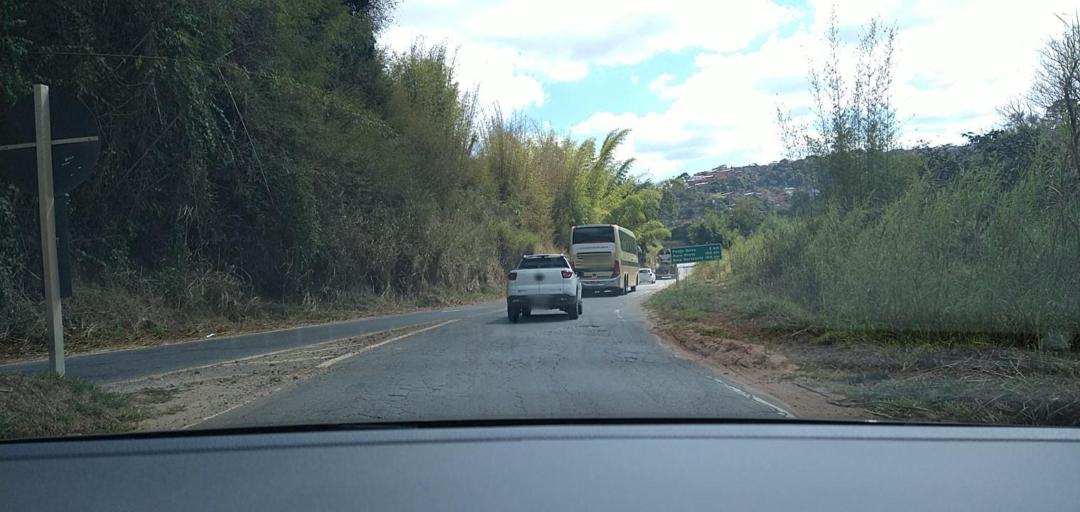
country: BR
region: Minas Gerais
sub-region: Ponte Nova
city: Ponte Nova
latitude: -20.4286
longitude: -42.8940
